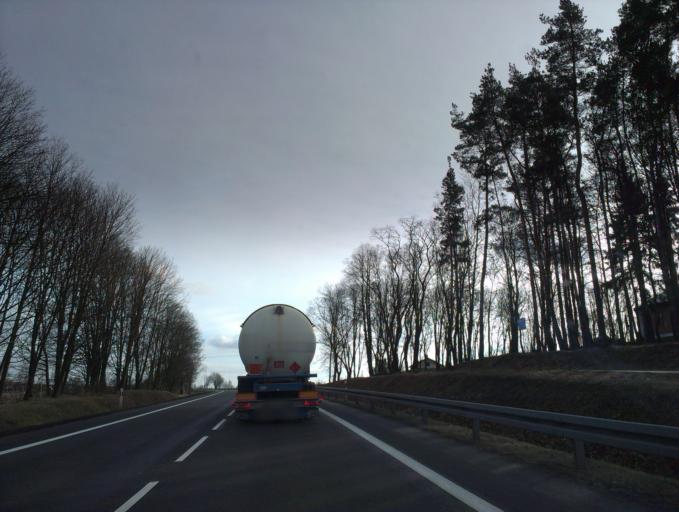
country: PL
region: Kujawsko-Pomorskie
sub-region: Powiat lipnowski
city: Kikol
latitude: 52.8929
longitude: 19.1245
